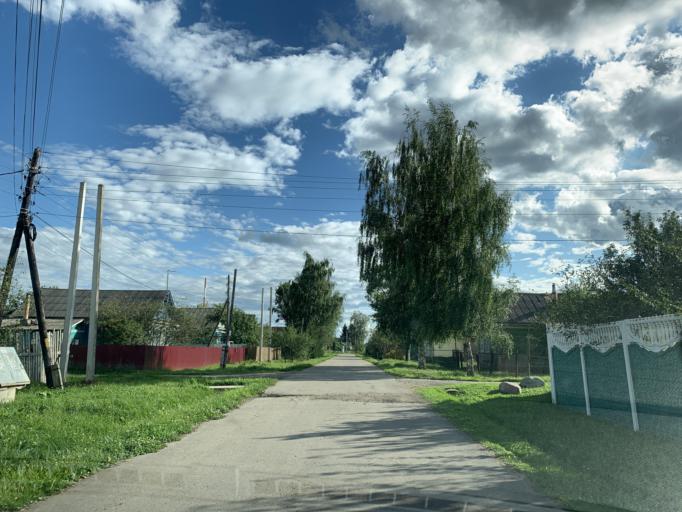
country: RU
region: Jaroslavl
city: Tunoshna
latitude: 57.6630
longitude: 40.0715
